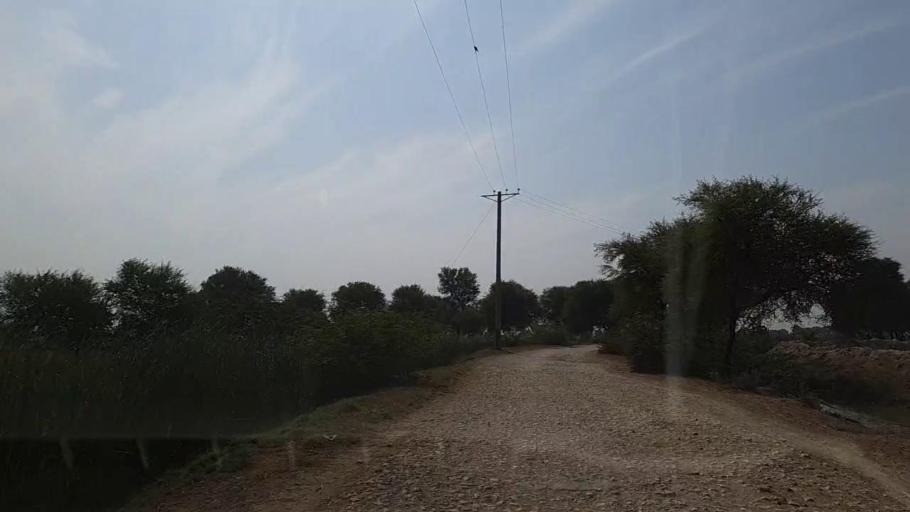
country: PK
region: Sindh
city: Mirpur Batoro
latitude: 24.6157
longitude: 68.2369
